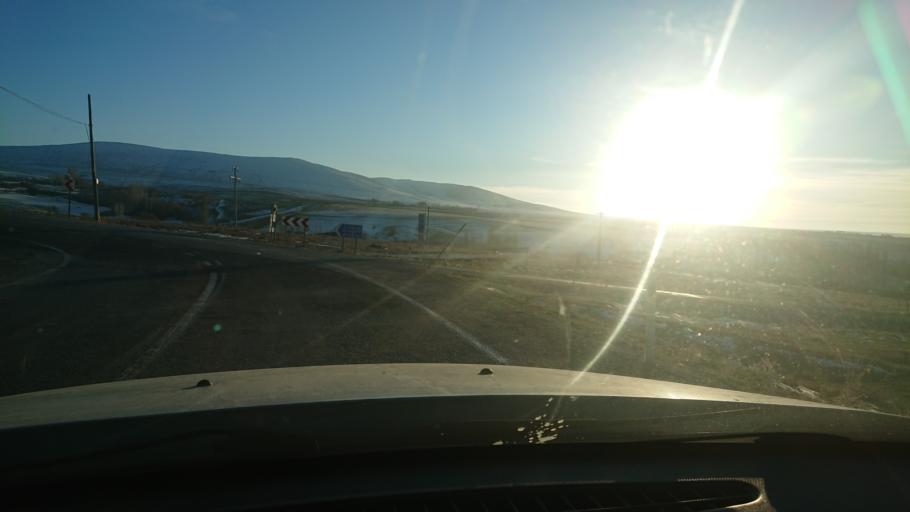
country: TR
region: Aksaray
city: Ortakoy
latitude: 38.7548
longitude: 33.9328
